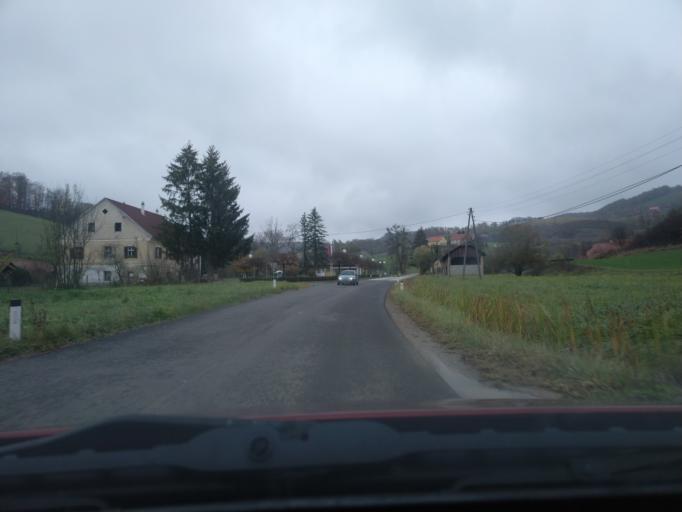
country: SI
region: Kungota
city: Zgornja Kungota
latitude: 46.6684
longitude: 15.6098
